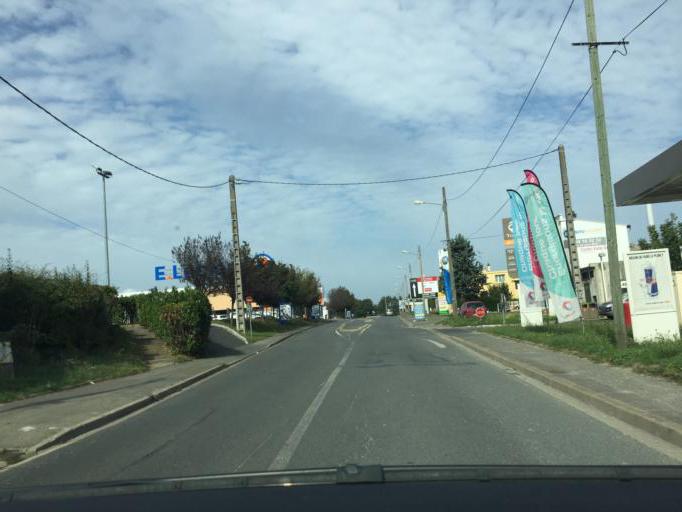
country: FR
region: Ile-de-France
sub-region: Departement de l'Essonne
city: Palaiseau
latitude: 48.7280
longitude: 2.2455
